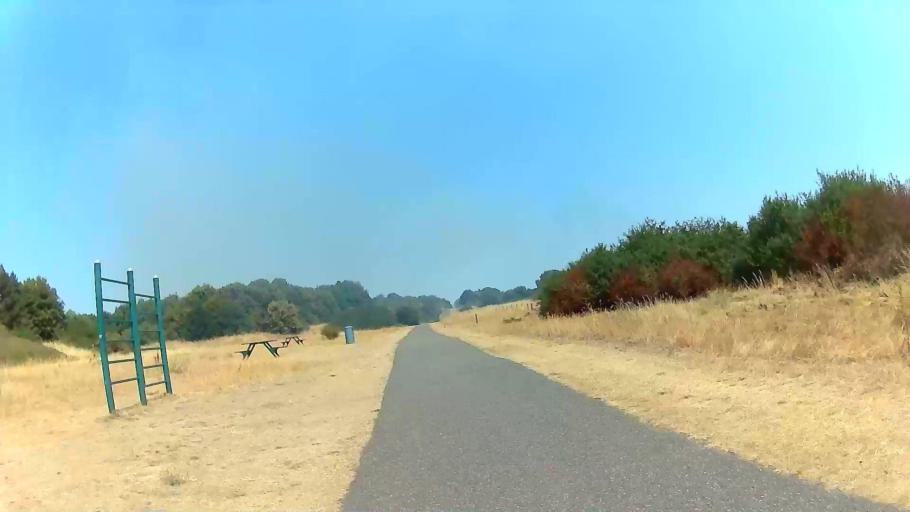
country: GB
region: England
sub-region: Greater London
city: Elm Park
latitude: 51.5344
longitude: 0.2125
